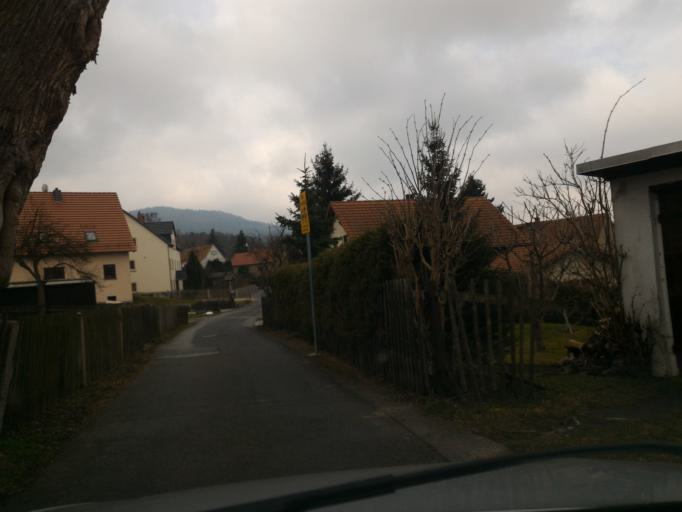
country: DE
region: Saxony
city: Olbersdorf
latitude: 50.8653
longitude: 14.7671
